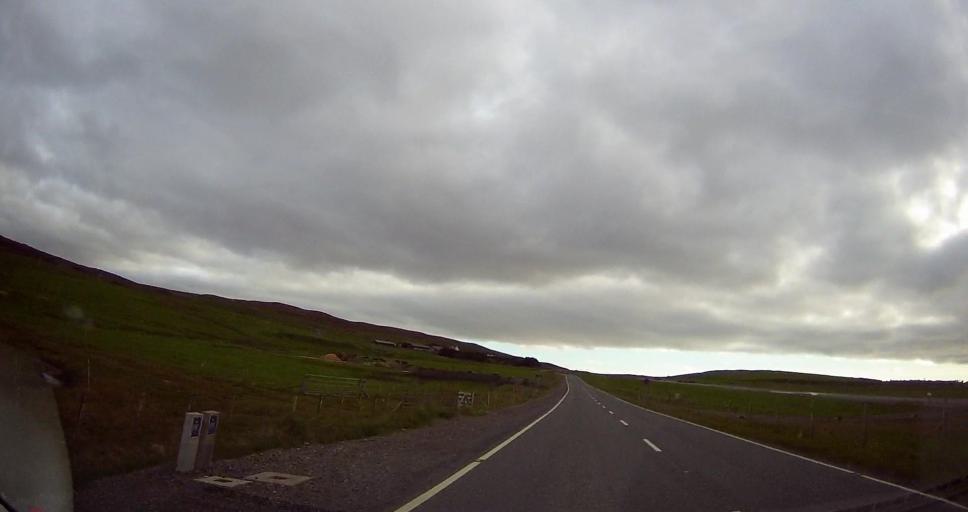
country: GB
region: Scotland
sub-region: Shetland Islands
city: Lerwick
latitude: 60.4349
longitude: -1.2874
